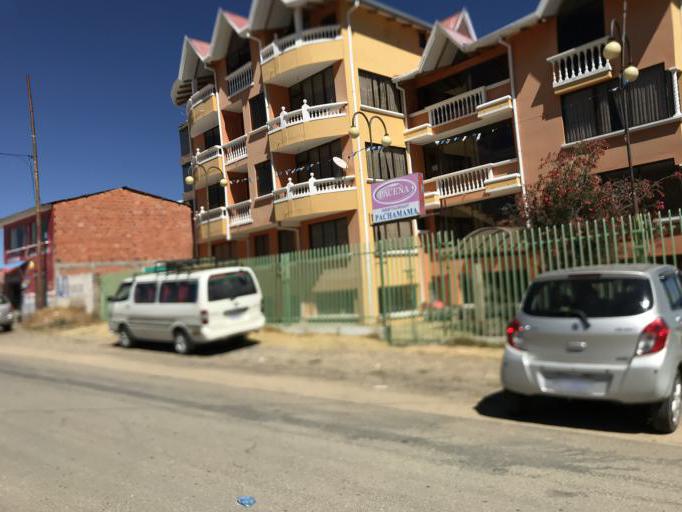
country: BO
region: La Paz
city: Huatajata
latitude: -16.2137
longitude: -68.6851
